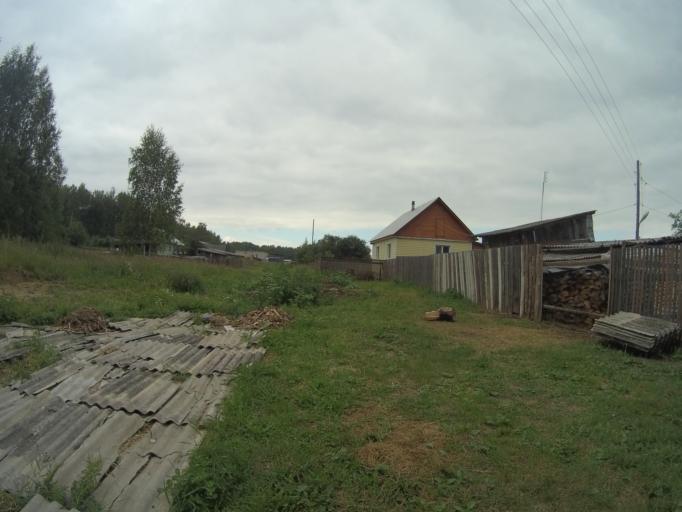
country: RU
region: Vladimir
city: Raduzhnyy
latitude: 55.9929
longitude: 40.2137
